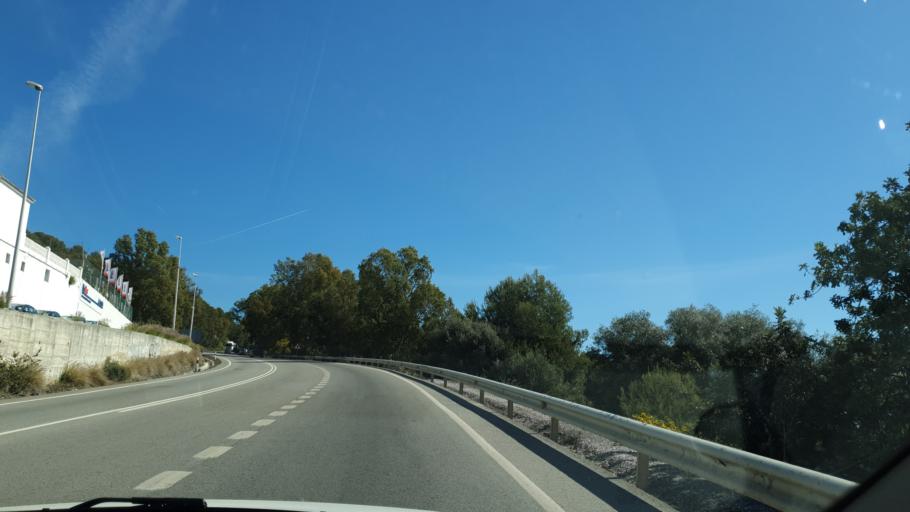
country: ES
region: Andalusia
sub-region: Provincia de Malaga
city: Marbella
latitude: 36.5290
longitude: -4.8799
